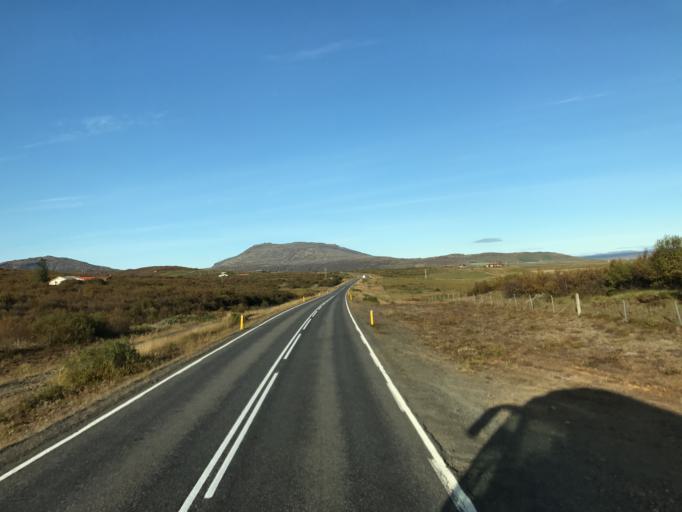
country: IS
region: South
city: Selfoss
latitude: 64.2529
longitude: -20.4881
